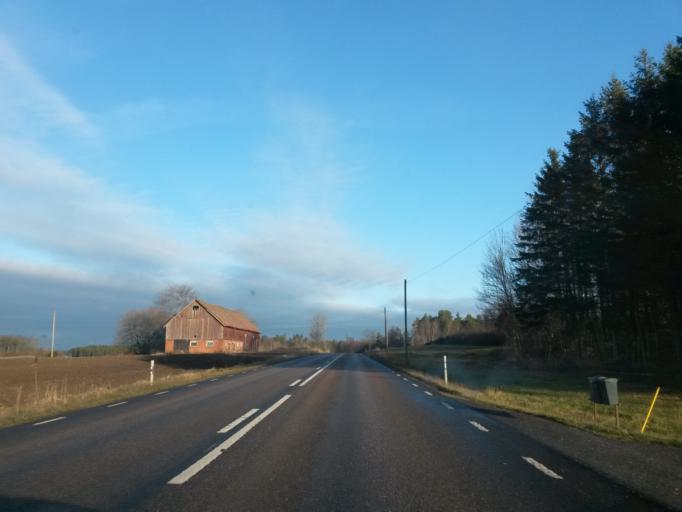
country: SE
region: Vaestra Goetaland
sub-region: Grastorps Kommun
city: Graestorp
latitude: 58.3818
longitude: 12.7465
